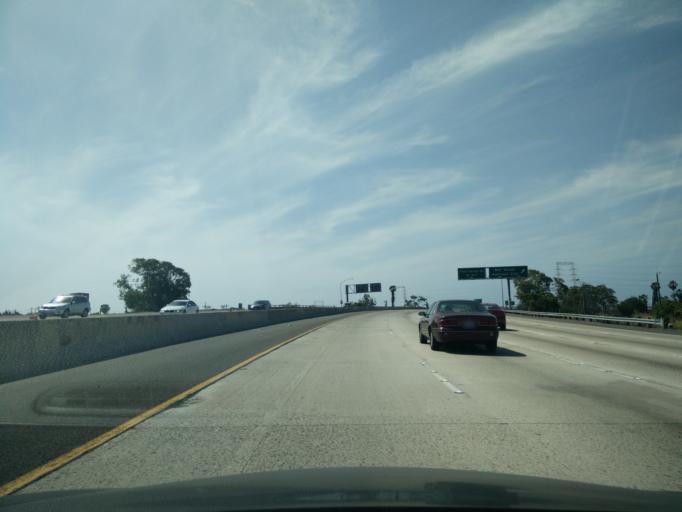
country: US
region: California
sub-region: San Diego County
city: National City
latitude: 32.6763
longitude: -117.1094
